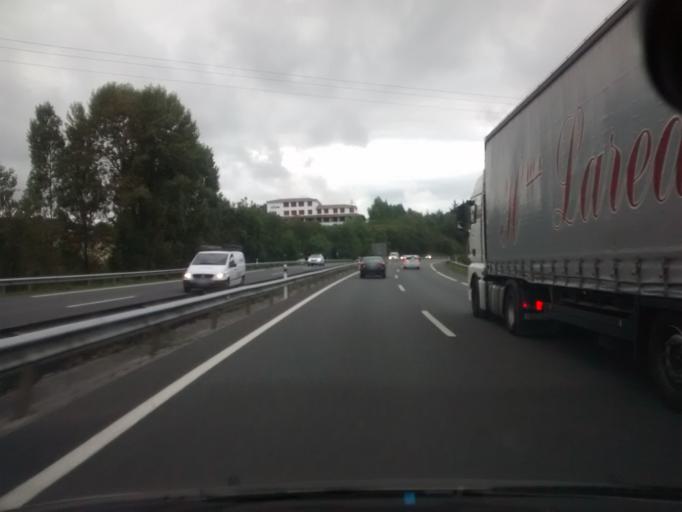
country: ES
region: Basque Country
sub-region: Provincia de Guipuzcoa
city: Zarautz
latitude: 43.2786
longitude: -2.1727
